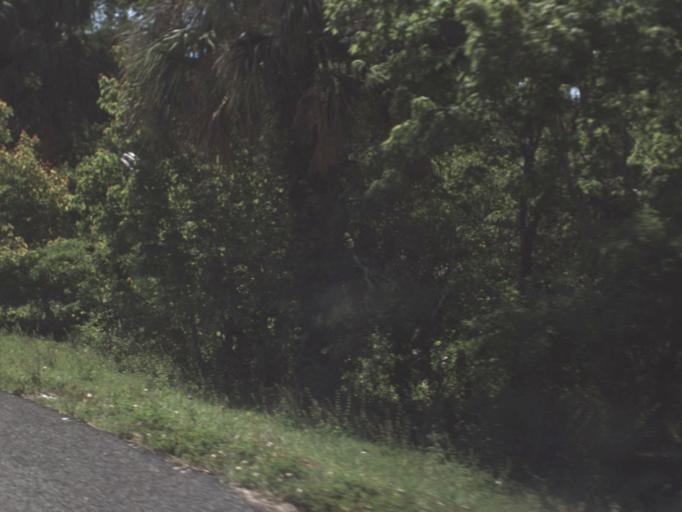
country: US
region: Florida
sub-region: Flagler County
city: Bunnell
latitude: 29.4084
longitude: -81.1996
